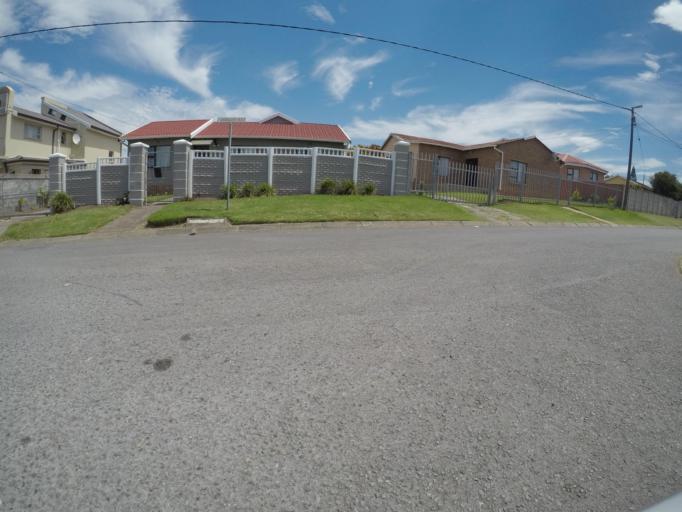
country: ZA
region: Eastern Cape
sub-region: Buffalo City Metropolitan Municipality
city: East London
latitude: -33.0427
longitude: 27.8643
